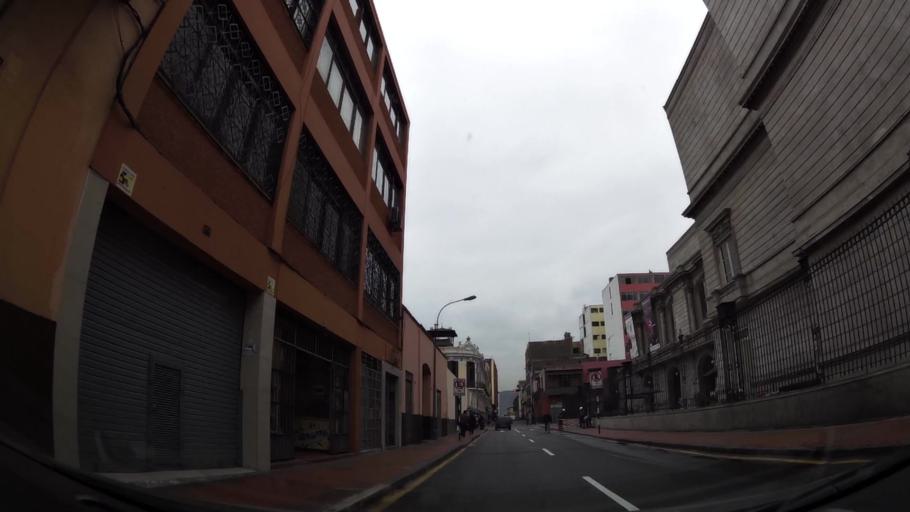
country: PE
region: Lima
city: Lima
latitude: -12.0456
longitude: -77.0354
